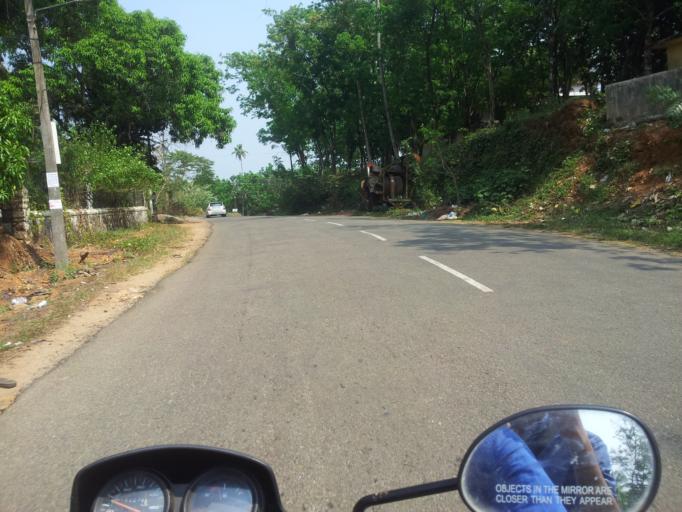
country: IN
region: Kerala
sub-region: Ernakulam
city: Muvattupuzha
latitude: 9.8952
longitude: 76.7020
